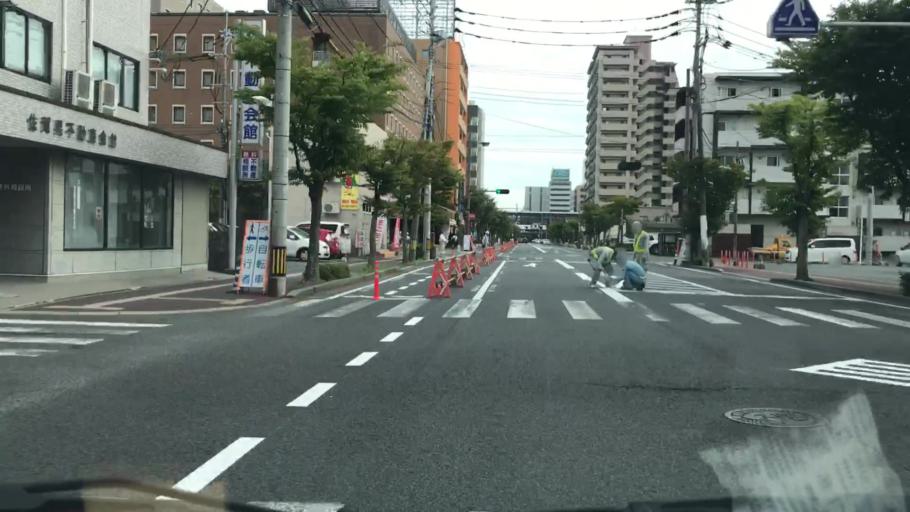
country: JP
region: Saga Prefecture
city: Saga-shi
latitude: 33.2676
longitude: 130.2967
